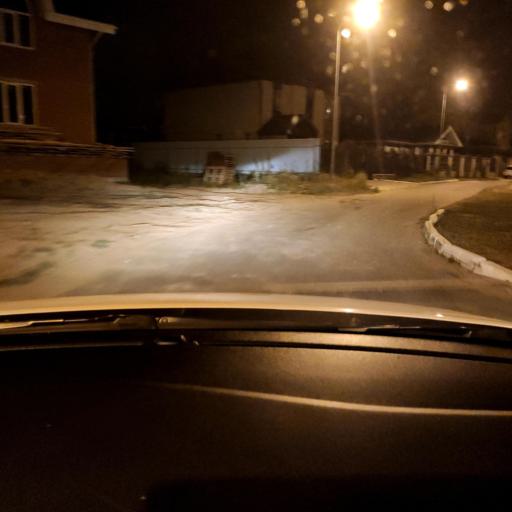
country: RU
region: Tatarstan
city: Osinovo
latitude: 55.8601
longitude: 48.7934
